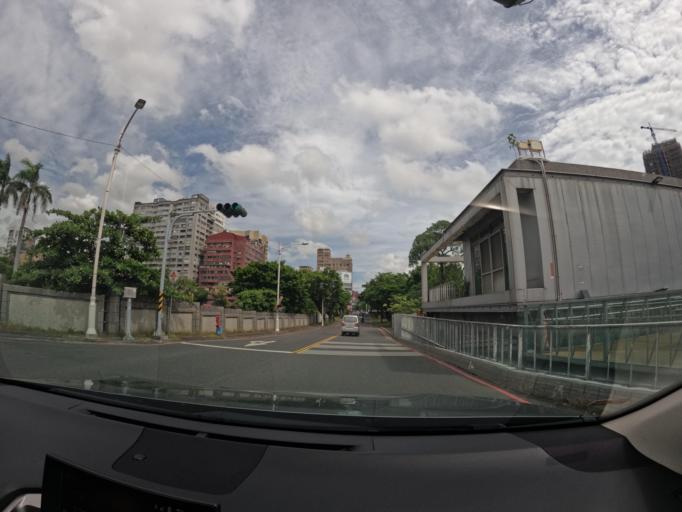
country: TW
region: Kaohsiung
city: Kaohsiung
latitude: 22.6319
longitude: 120.2865
